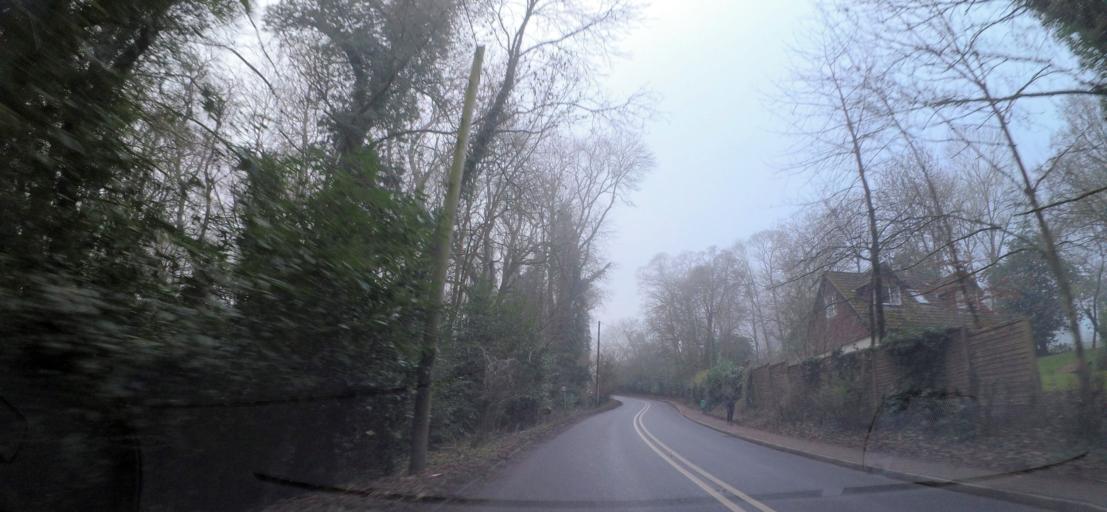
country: GB
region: England
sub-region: West Berkshire
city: Stratfield Mortimer
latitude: 51.4061
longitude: -1.0442
